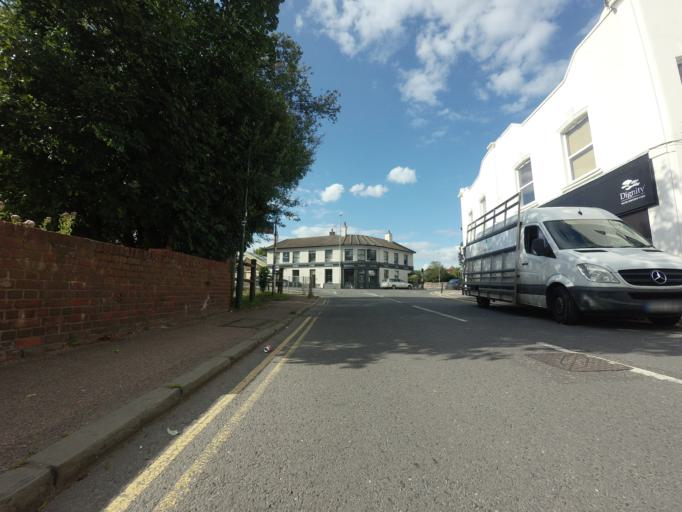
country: GB
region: England
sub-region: East Sussex
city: Hailsham
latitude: 50.8615
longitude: 0.2575
